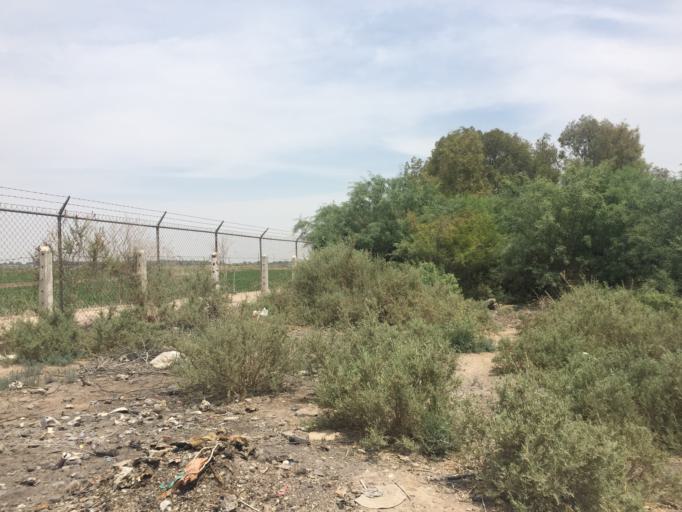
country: MX
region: Durango
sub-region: Gomez Palacio
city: San Jose de Vinedo
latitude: 25.6649
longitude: -103.4268
